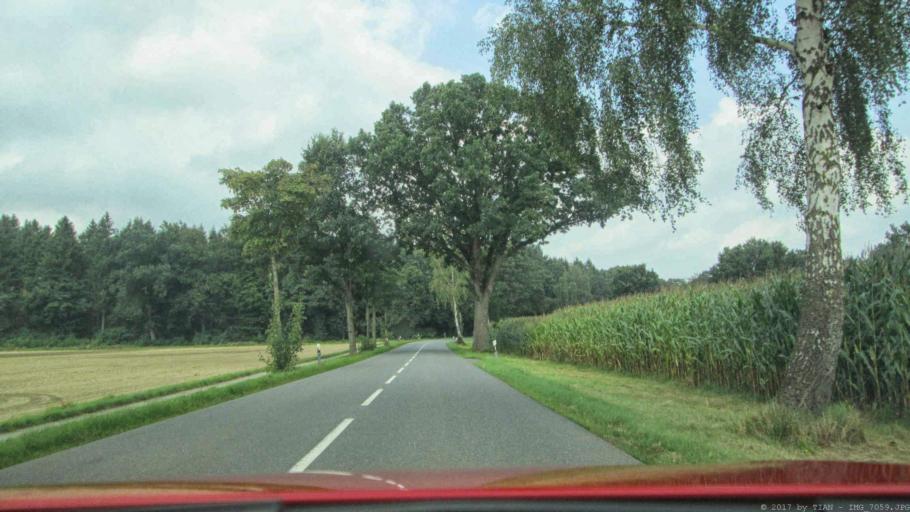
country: DE
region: Lower Saxony
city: Thomasburg
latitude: 53.2158
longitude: 10.6491
